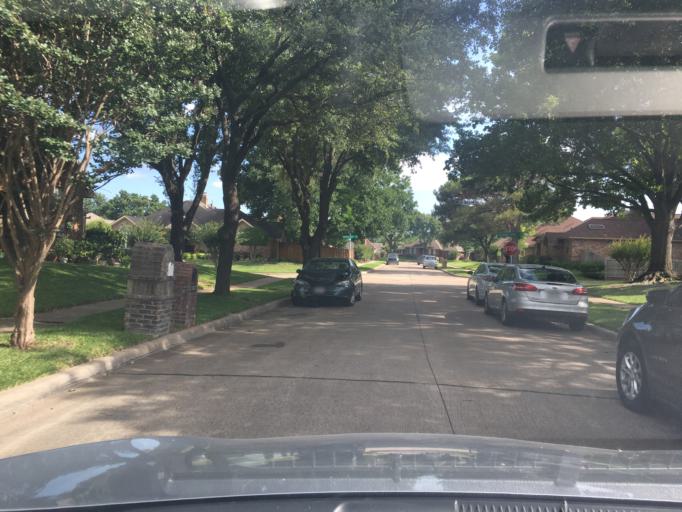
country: US
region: Texas
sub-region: Dallas County
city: Garland
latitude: 32.9329
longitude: -96.6747
